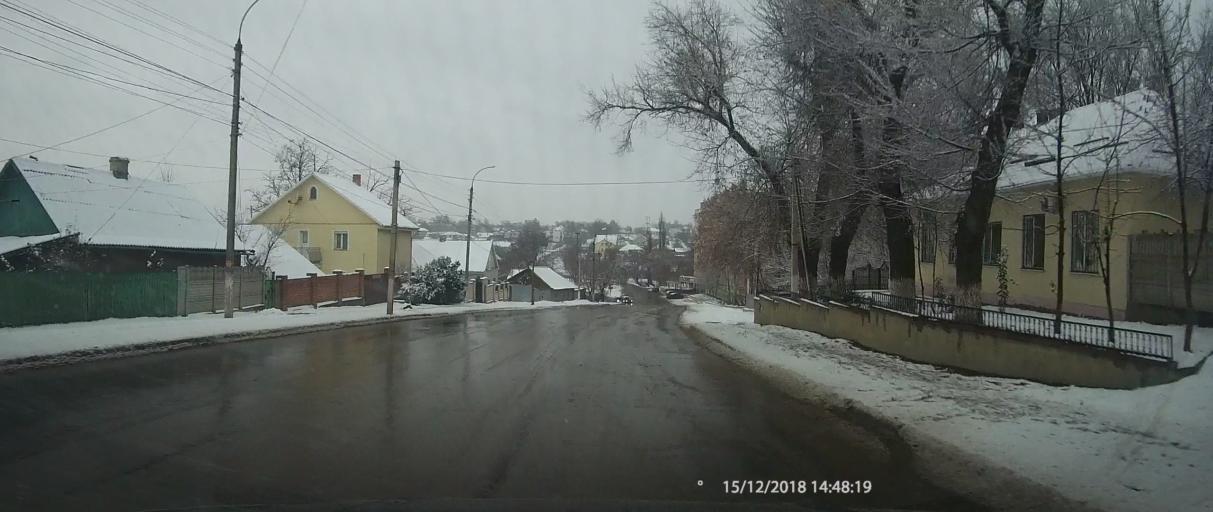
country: MD
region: Cahul
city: Cahul
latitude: 45.8964
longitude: 28.1985
